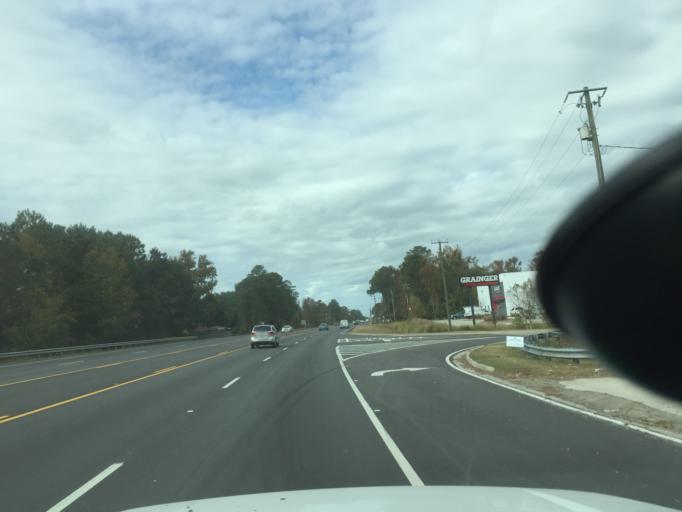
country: US
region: Georgia
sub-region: Chatham County
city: Garden City
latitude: 32.0859
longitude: -81.1654
